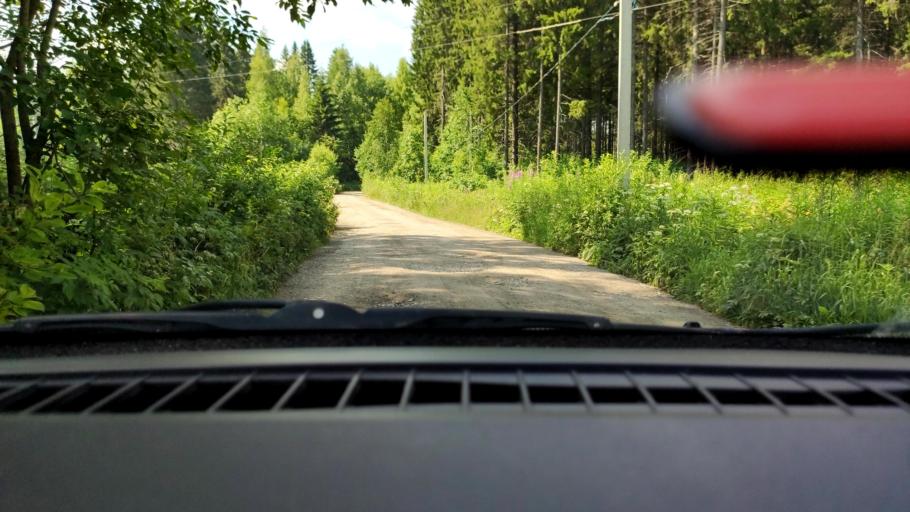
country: RU
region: Perm
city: Perm
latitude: 58.1479
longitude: 56.2958
